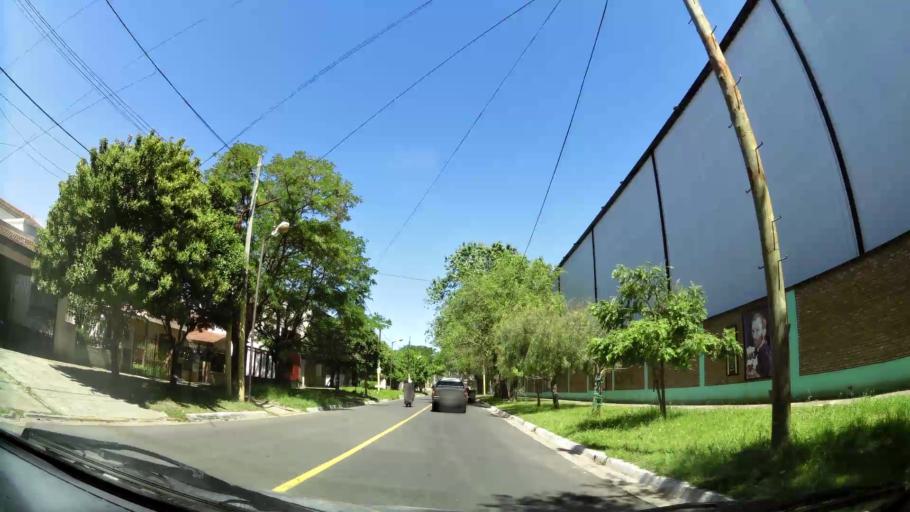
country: AR
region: Buenos Aires
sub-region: Partido de Quilmes
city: Quilmes
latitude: -34.7256
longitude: -58.2837
